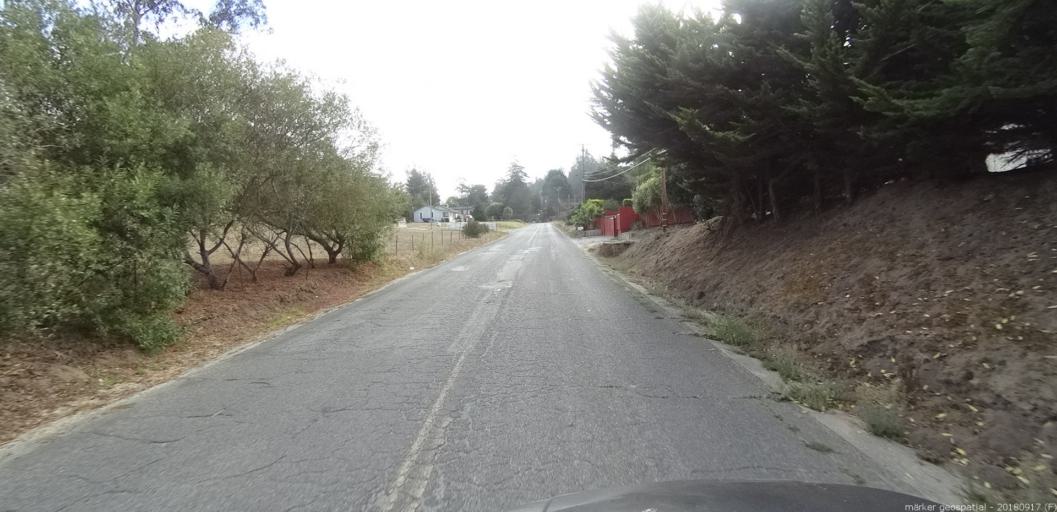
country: US
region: California
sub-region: Monterey County
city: Elkhorn
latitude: 36.8154
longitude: -121.6992
